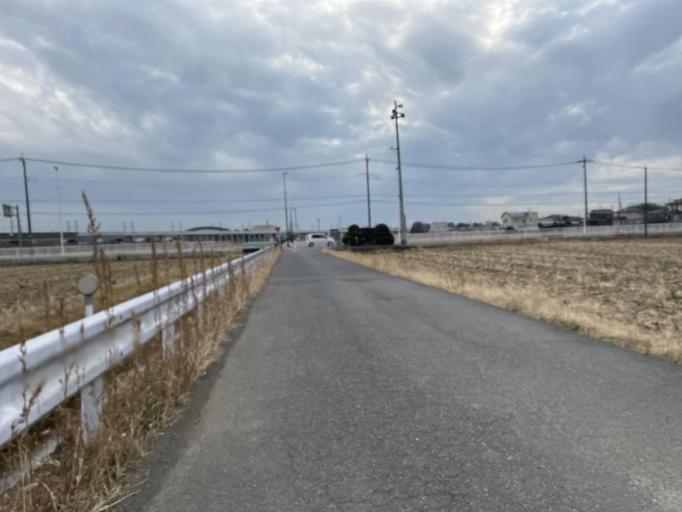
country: JP
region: Saitama
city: Shiraoka
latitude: 36.0167
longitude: 139.6468
